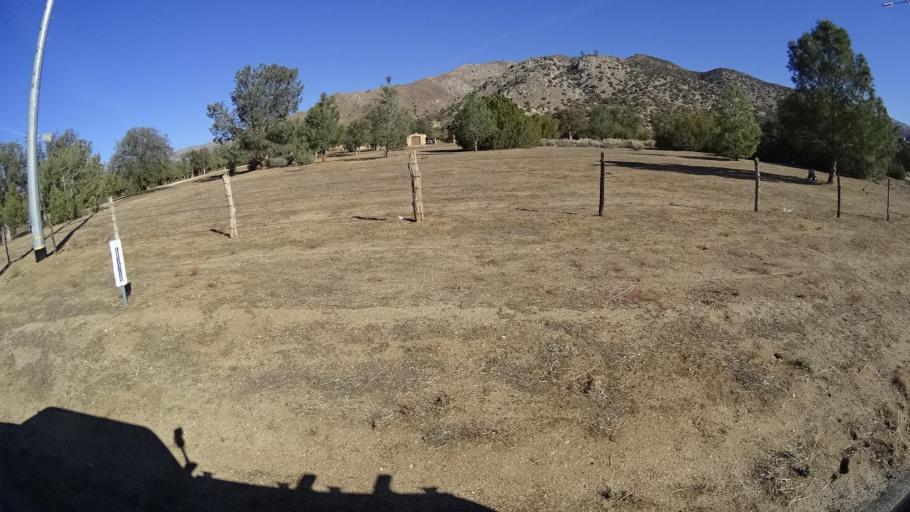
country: US
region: California
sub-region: Kern County
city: Bodfish
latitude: 35.4022
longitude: -118.4778
